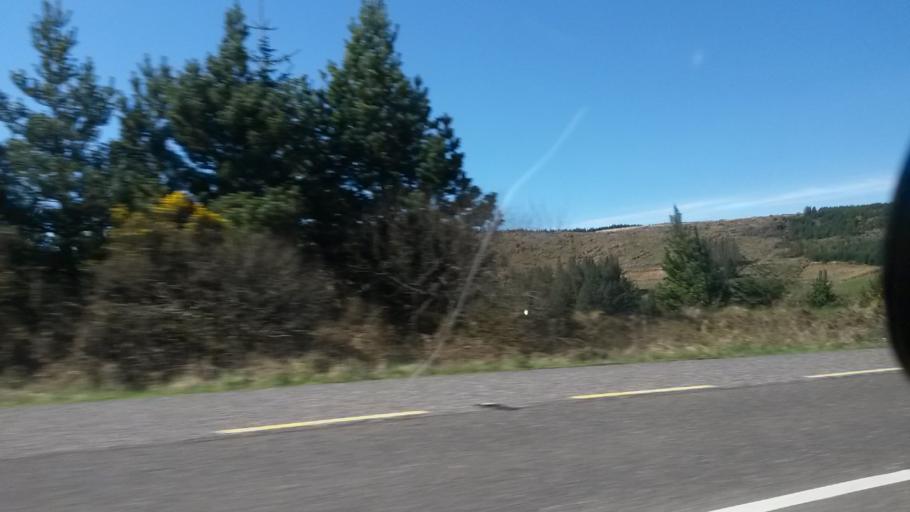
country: IE
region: Munster
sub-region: County Cork
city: Millstreet
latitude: 51.9612
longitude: -9.2402
